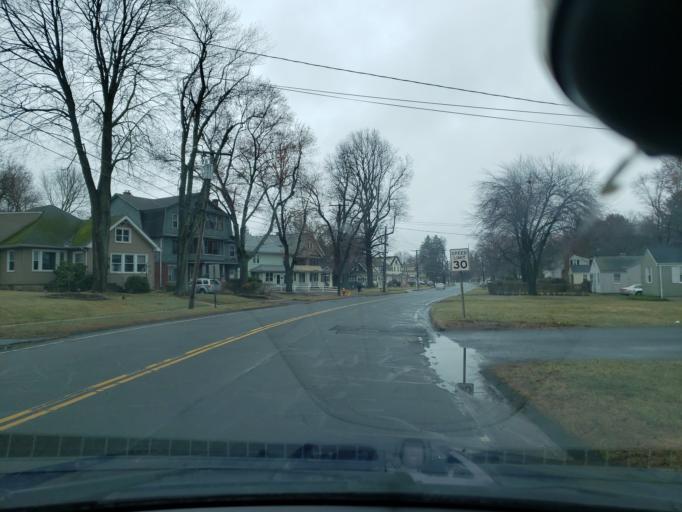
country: US
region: Connecticut
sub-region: Hartford County
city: Windsor
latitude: 41.8267
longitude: -72.6544
